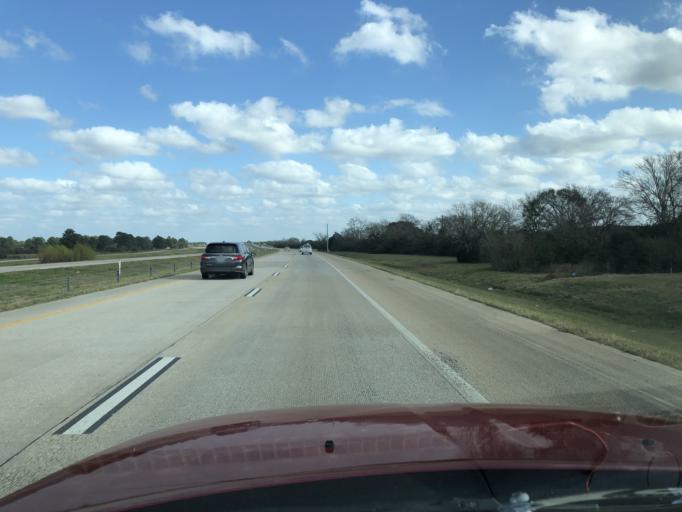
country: US
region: Texas
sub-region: Harris County
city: Cypress
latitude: 30.0503
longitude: -95.6893
